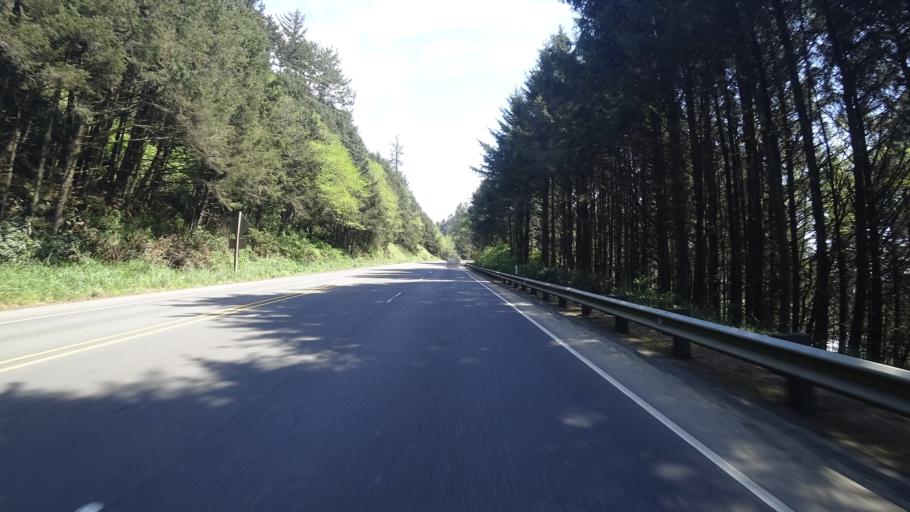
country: US
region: Oregon
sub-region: Lincoln County
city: Depoe Bay
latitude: 44.7802
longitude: -124.0721
